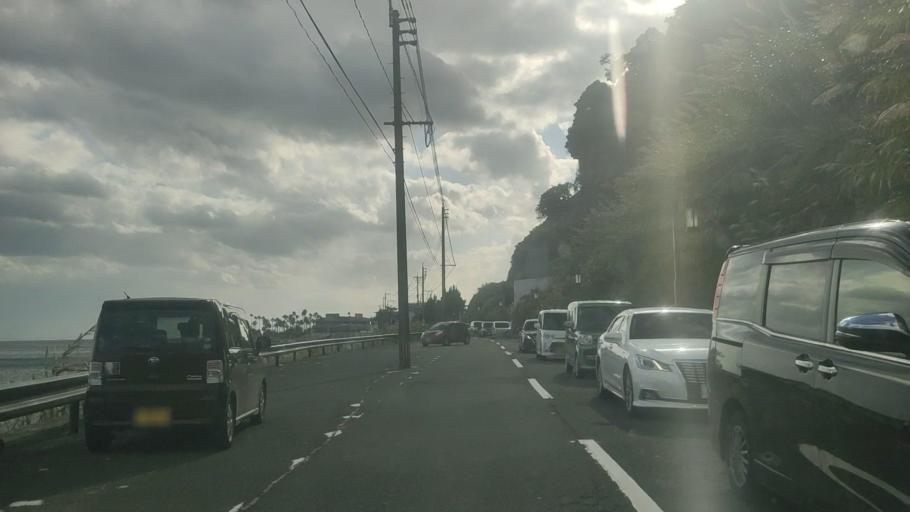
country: JP
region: Kagoshima
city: Kagoshima-shi
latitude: 31.6117
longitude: 130.5752
